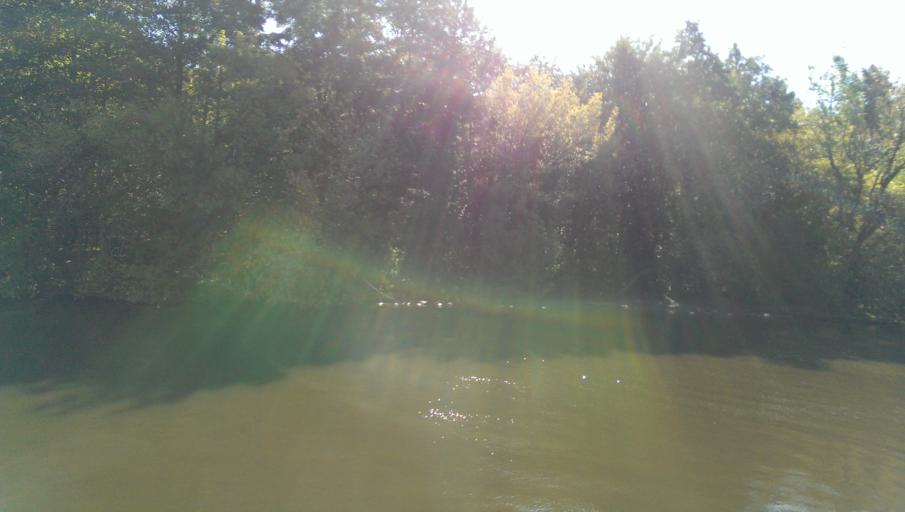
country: DE
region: Berlin
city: Wannsee
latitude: 52.4119
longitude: 13.1542
